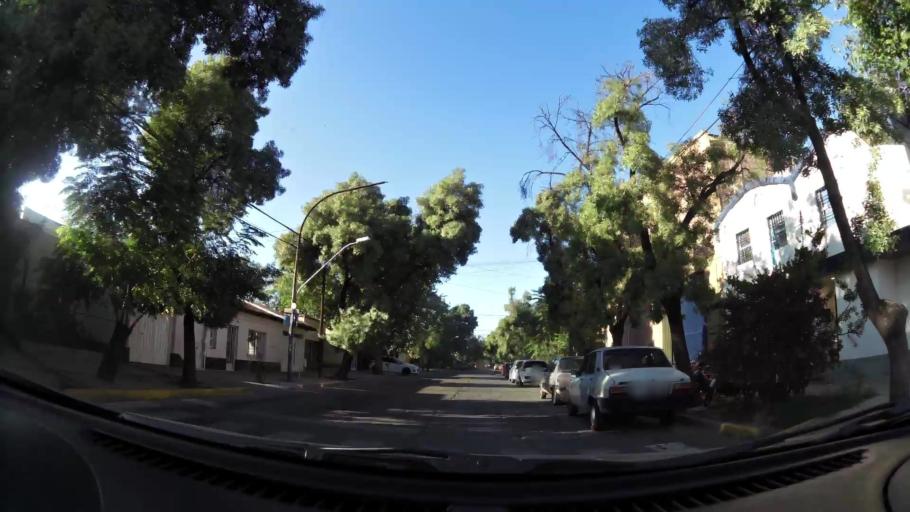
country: AR
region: Mendoza
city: Las Heras
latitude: -32.8695
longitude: -68.8230
